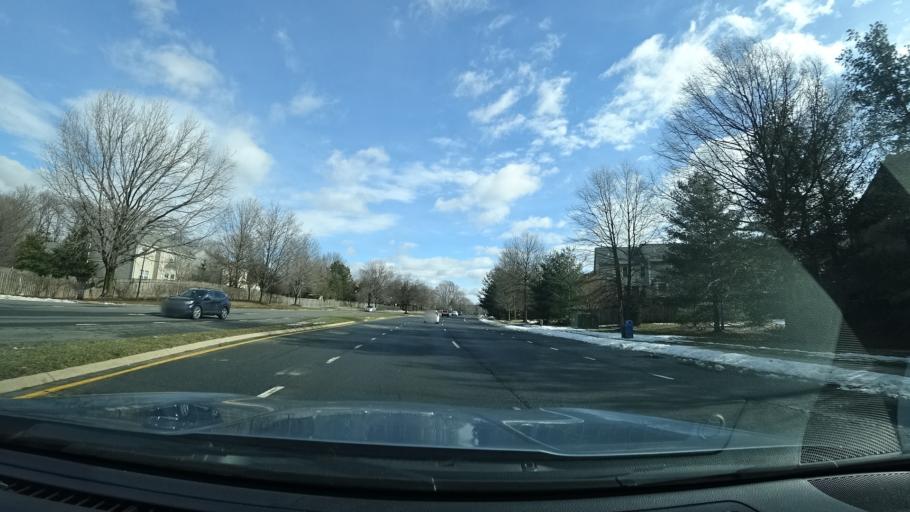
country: US
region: Virginia
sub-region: Loudoun County
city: Sugarland Run
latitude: 39.0354
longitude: -77.3912
